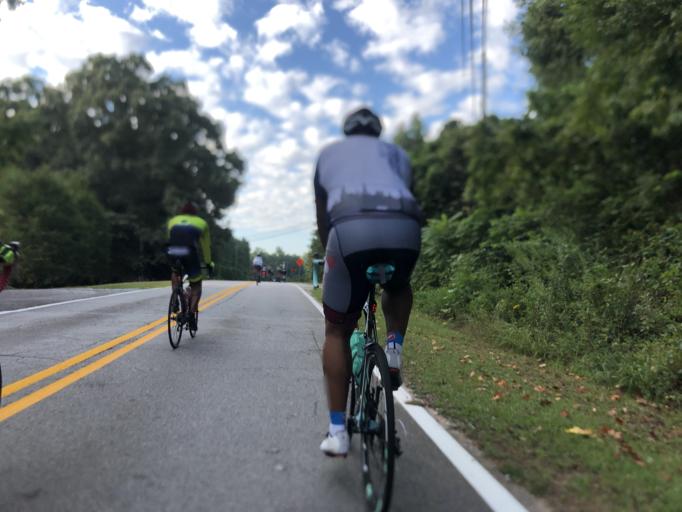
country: US
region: Georgia
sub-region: Fulton County
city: Palmetto
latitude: 33.5881
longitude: -84.6521
